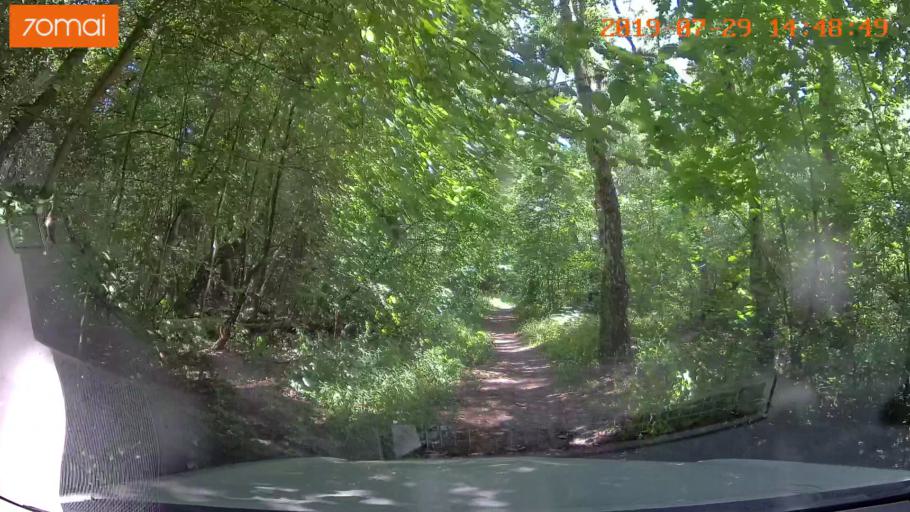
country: RU
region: Kaliningrad
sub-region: Gorod Kaliningrad
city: Baltiysk
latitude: 54.6633
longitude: 19.9023
